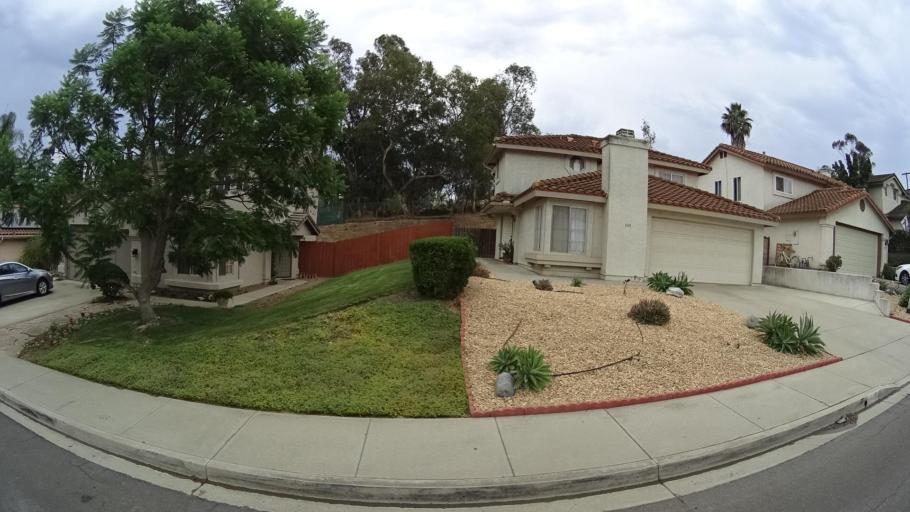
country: US
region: California
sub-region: San Diego County
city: Escondido
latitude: 33.1462
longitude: -117.1126
